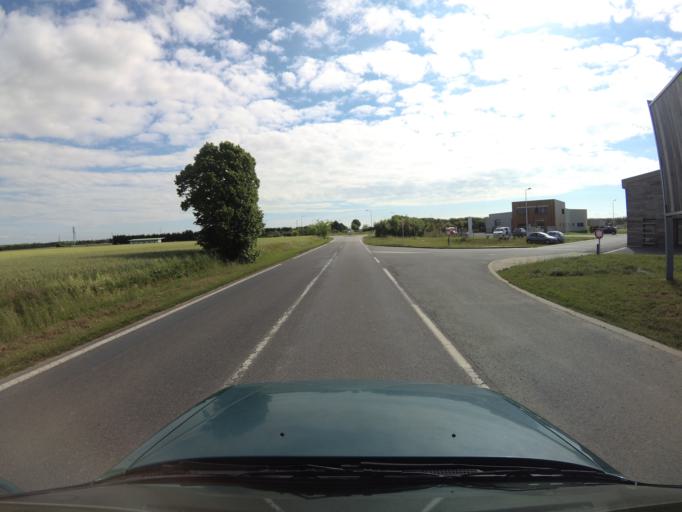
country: FR
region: Poitou-Charentes
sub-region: Departement de la Charente-Maritime
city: Saint-Xandre
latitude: 46.2355
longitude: -1.0727
